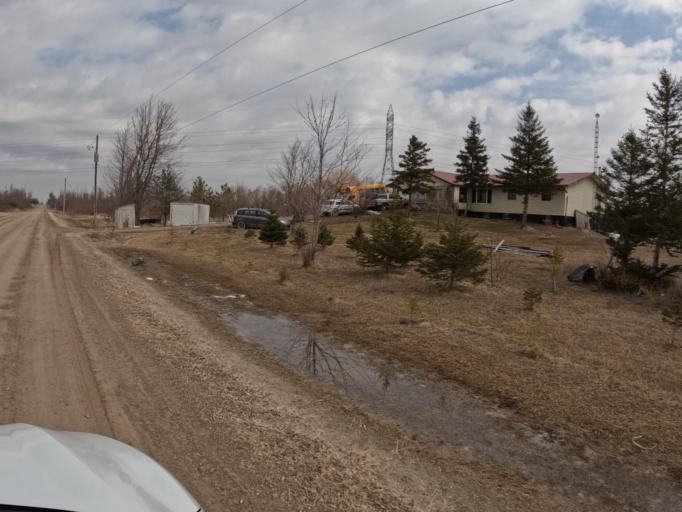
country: CA
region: Ontario
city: Orangeville
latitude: 43.9336
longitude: -80.2209
